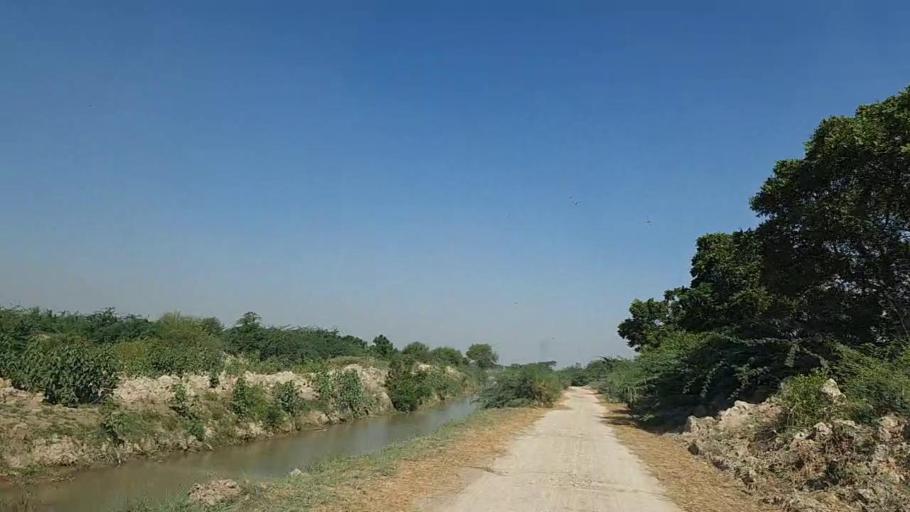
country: PK
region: Sindh
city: Daro Mehar
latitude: 24.7655
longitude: 68.1551
